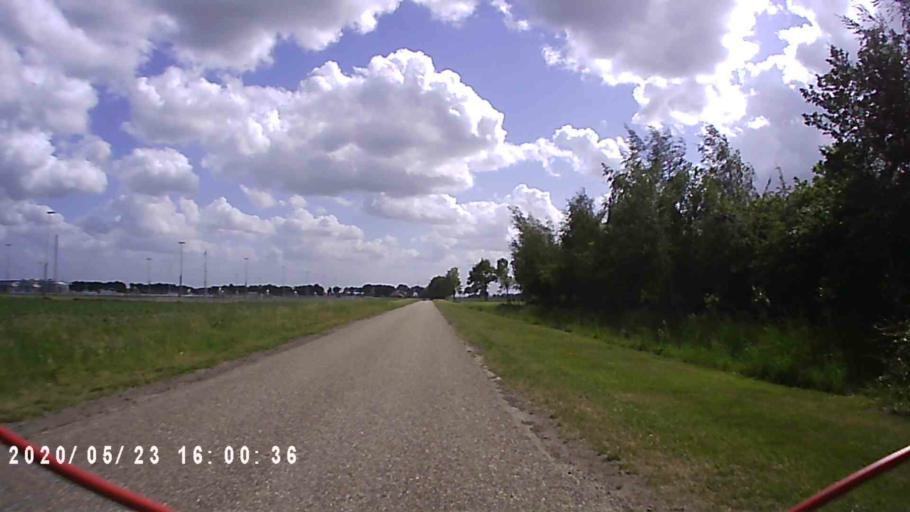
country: NL
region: Groningen
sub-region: Gemeente Delfzijl
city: Delfzijl
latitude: 53.2517
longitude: 6.9001
